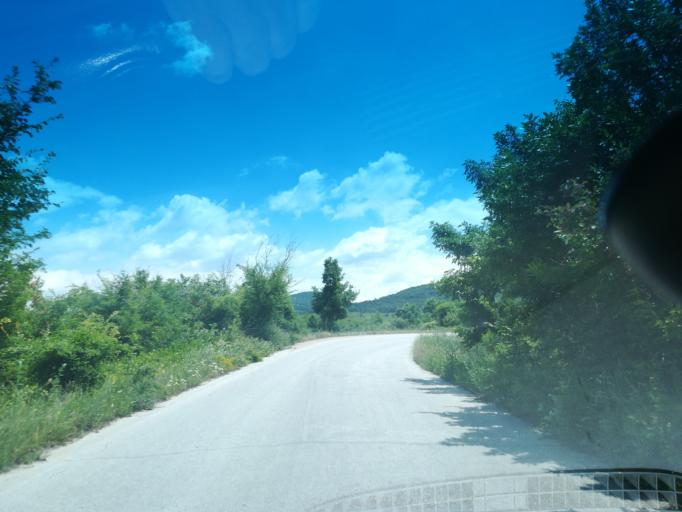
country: BG
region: Khaskovo
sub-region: Obshtina Mineralni Bani
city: Mineralni Bani
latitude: 41.9843
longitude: 25.2469
